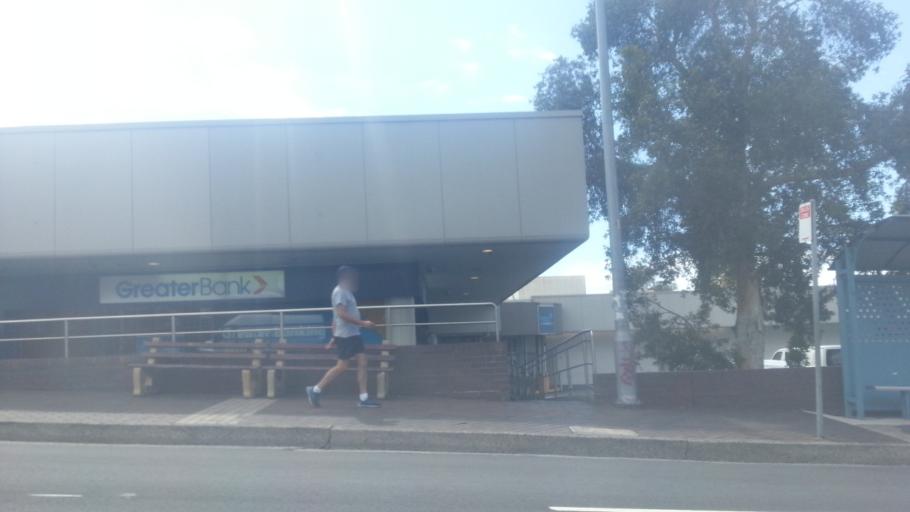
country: AU
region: New South Wales
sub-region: Wollongong
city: Corrimal
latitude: -34.3739
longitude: 150.8968
